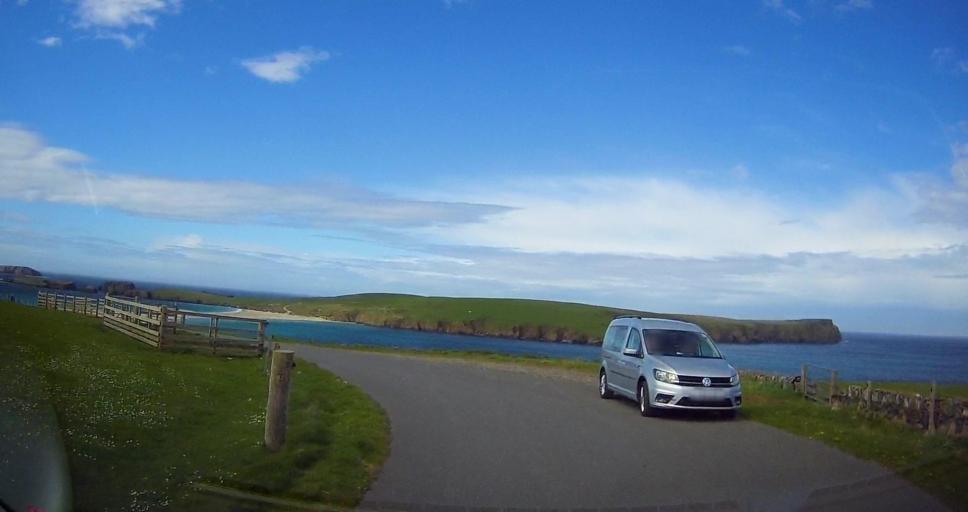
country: GB
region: Scotland
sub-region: Shetland Islands
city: Sandwick
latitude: 59.9731
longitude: -1.3266
